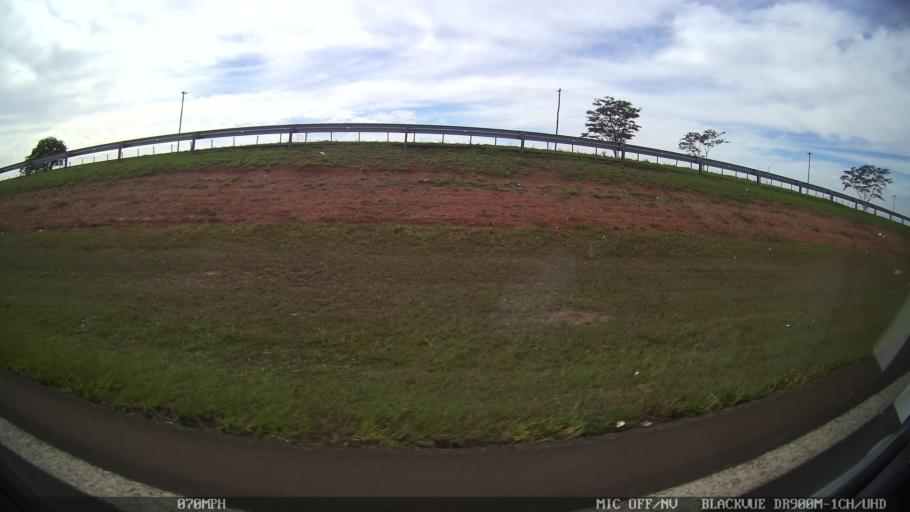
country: BR
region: Sao Paulo
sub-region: Taquaritinga
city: Taquaritinga
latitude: -21.5444
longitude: -48.4986
